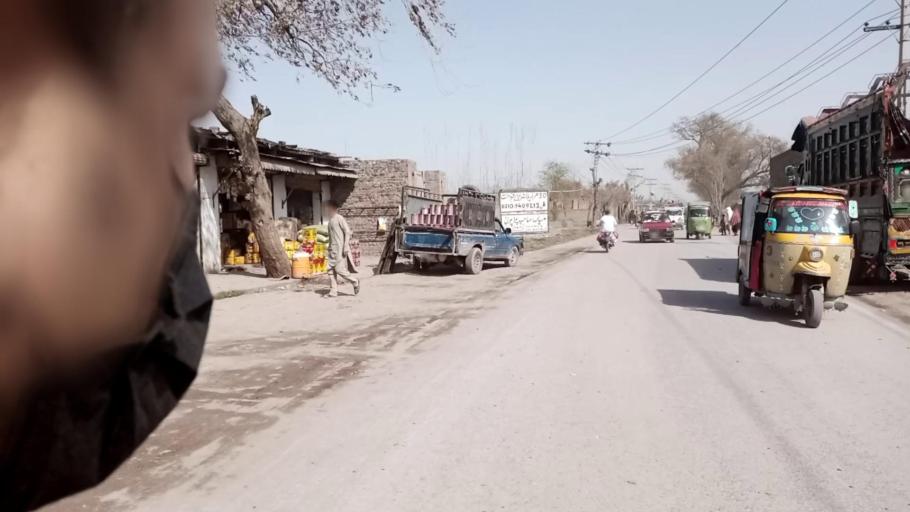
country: PK
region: Khyber Pakhtunkhwa
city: Peshawar
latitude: 33.9969
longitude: 71.6340
